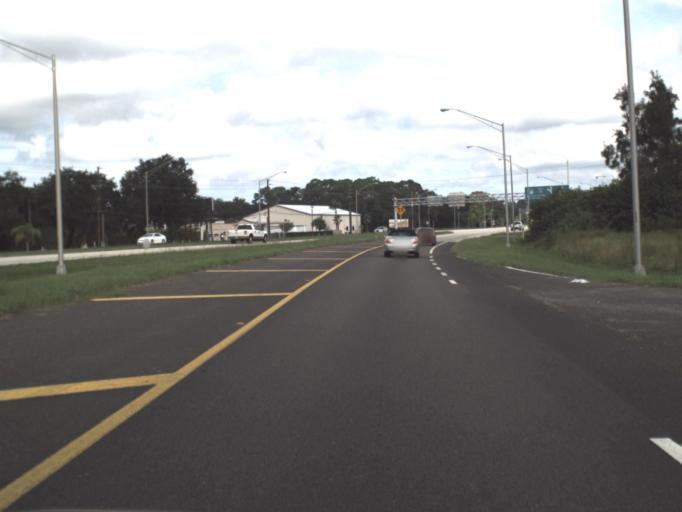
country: US
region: Florida
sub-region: Manatee County
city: Memphis
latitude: 27.5431
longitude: -82.5640
